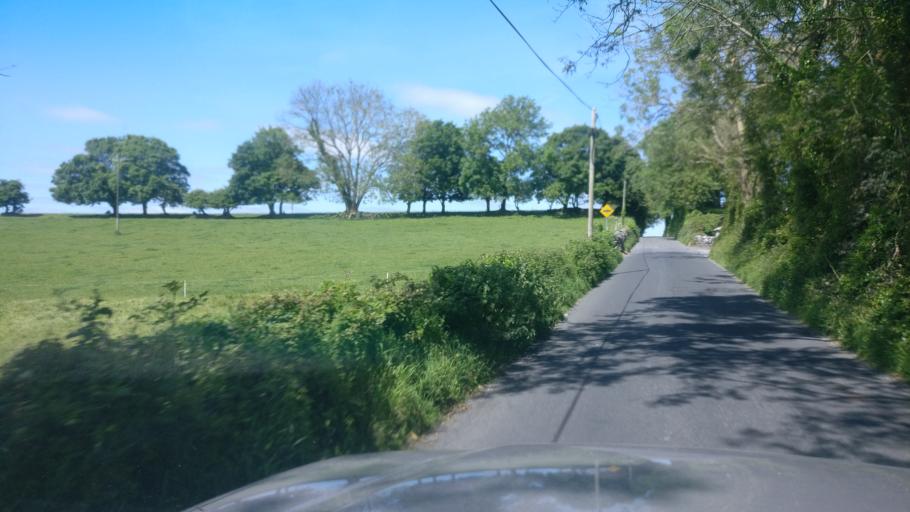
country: IE
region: Connaught
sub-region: County Galway
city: Gort
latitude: 53.0953
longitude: -8.8135
